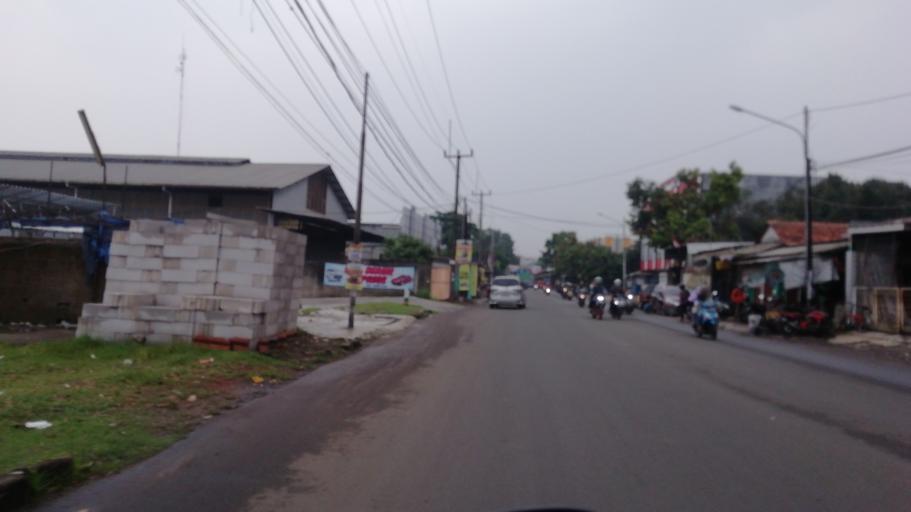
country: ID
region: West Java
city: Cibinong
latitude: -6.5305
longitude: 106.8099
